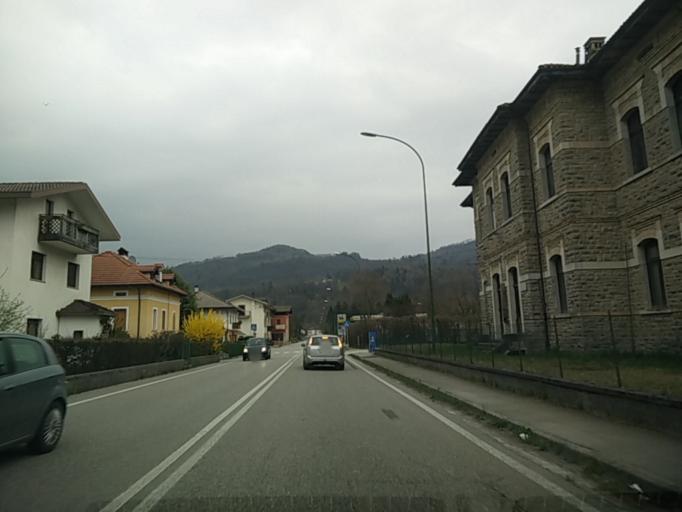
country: IT
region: Veneto
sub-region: Provincia di Belluno
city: Castion
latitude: 46.1508
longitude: 12.2559
